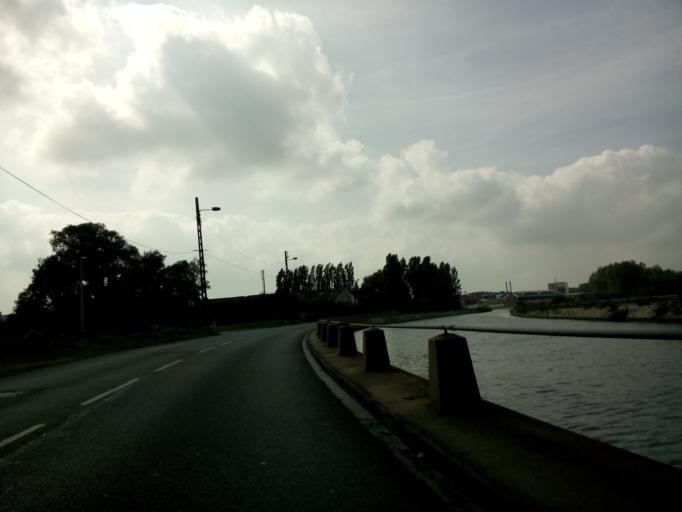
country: FR
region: Nord-Pas-de-Calais
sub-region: Departement du Pas-de-Calais
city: Coulogne
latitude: 50.9359
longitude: 1.8720
